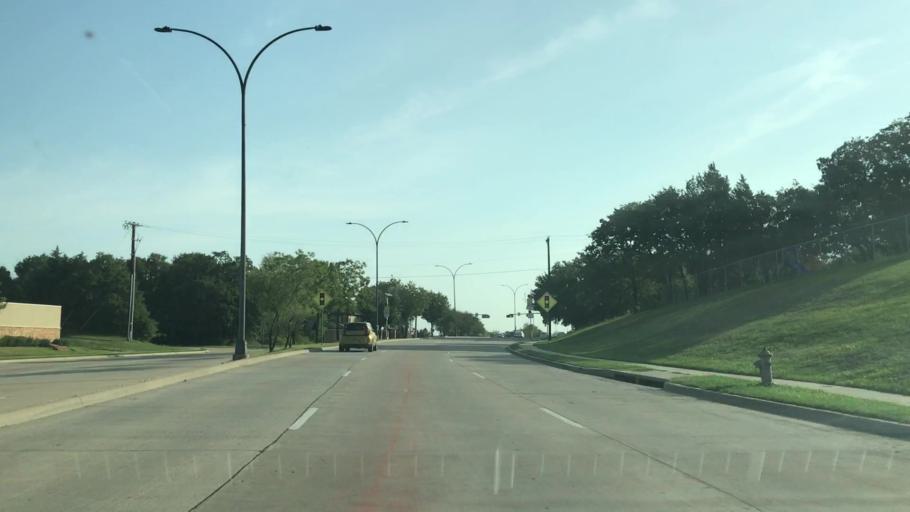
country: US
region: Texas
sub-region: Tarrant County
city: Arlington
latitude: 32.7779
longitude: -97.0742
